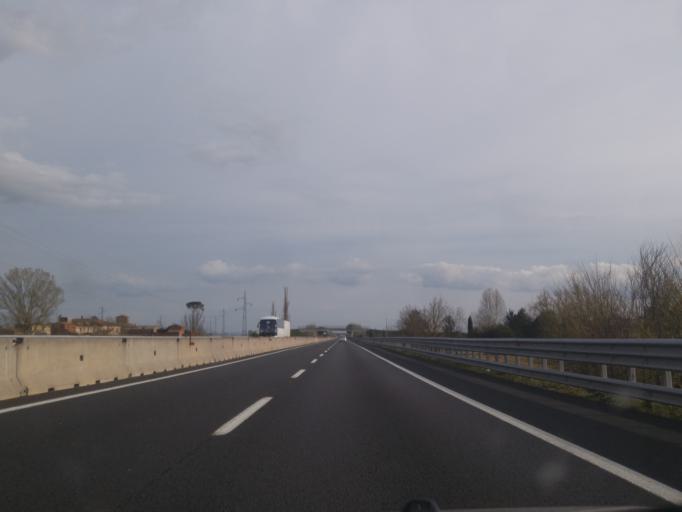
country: IT
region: Tuscany
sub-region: Provincia di Siena
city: Bettolle
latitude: 43.1852
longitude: 11.8269
